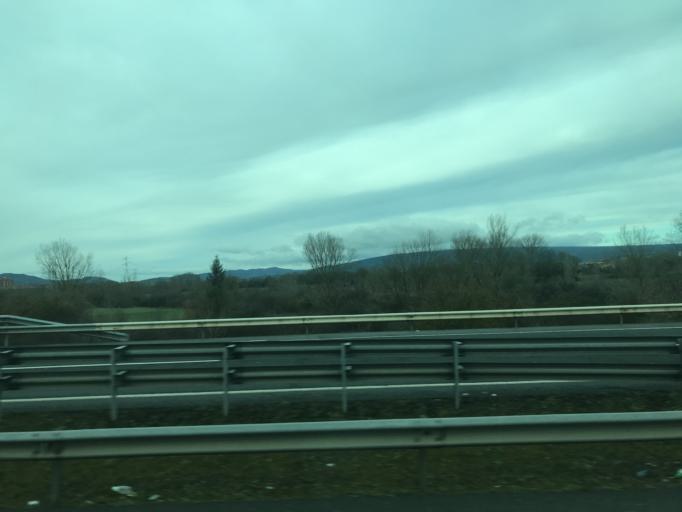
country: ES
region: Basque Country
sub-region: Provincia de Alava
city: Gasteiz / Vitoria
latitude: 42.8758
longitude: -2.6928
